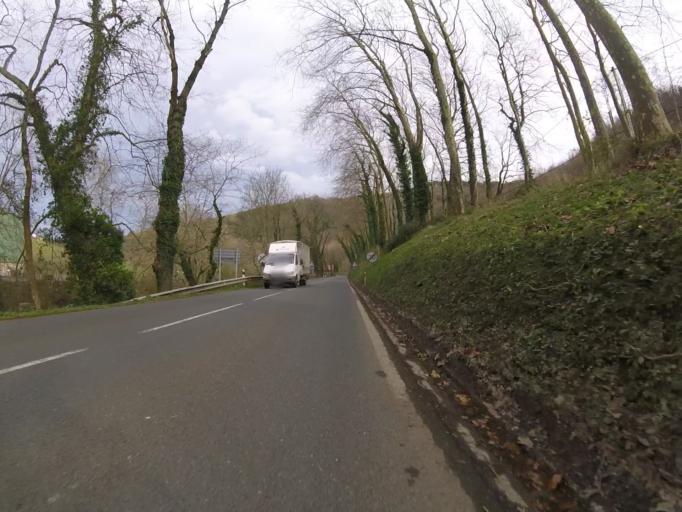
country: ES
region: Basque Country
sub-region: Provincia de Guipuzcoa
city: Aizarnazabal
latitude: 43.2540
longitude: -2.2334
